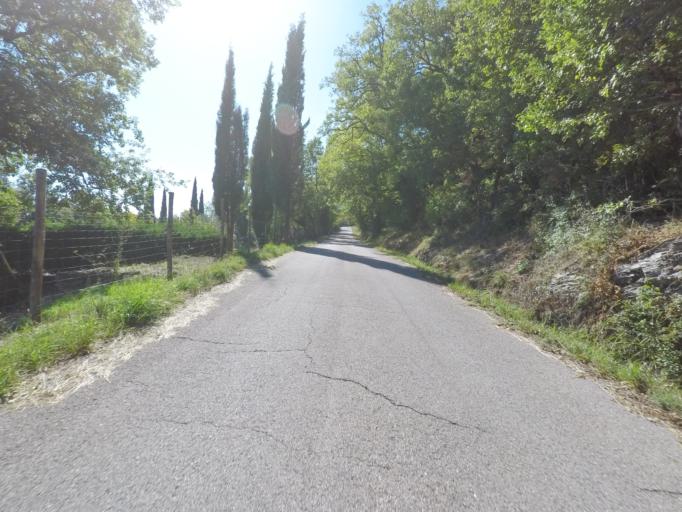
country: IT
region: Tuscany
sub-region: Provincia di Siena
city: Castellina in Chianti
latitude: 43.4292
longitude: 11.3356
